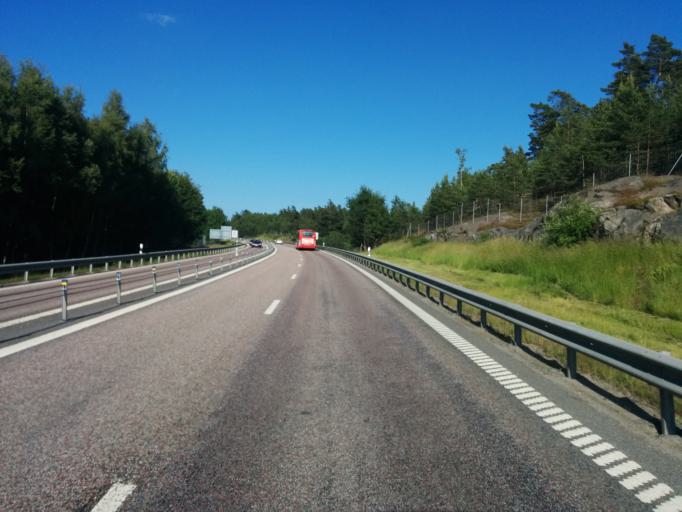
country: SE
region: Stockholm
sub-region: Varmdo Kommun
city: Gustavsberg
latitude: 59.3054
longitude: 18.4047
